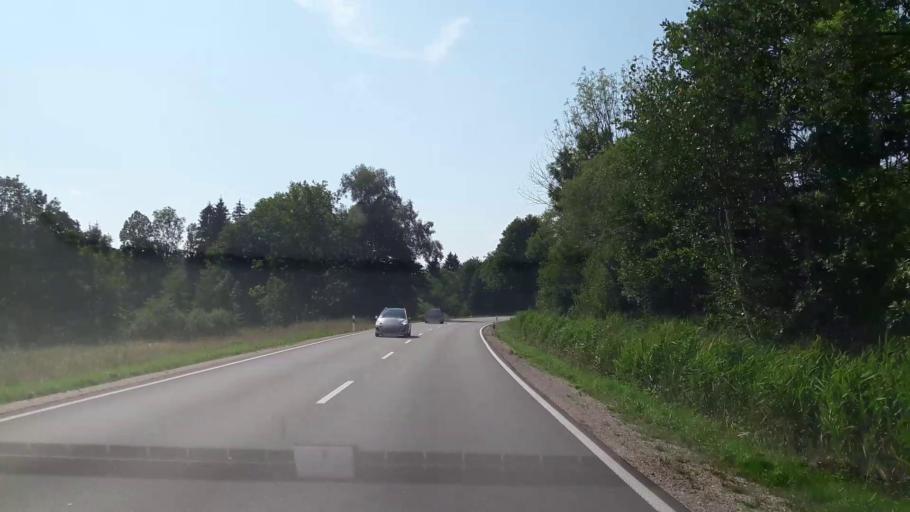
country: DE
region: Bavaria
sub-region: Upper Bavaria
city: Surberg
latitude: 47.8649
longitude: 12.7320
